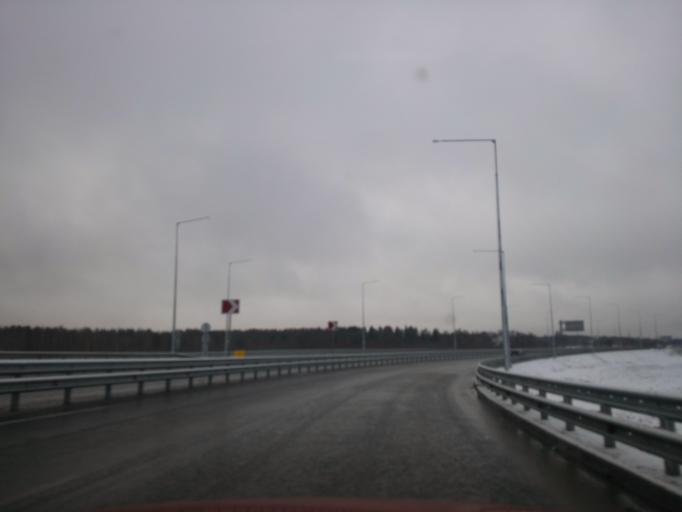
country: RU
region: Tverskaya
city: Likhoslavl'
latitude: 56.9496
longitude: 35.5137
